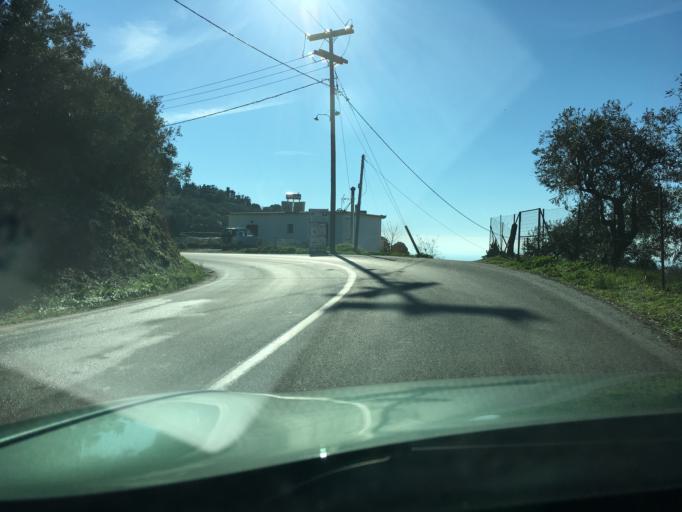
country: GR
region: Thessaly
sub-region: Nomos Magnisias
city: Skopelos
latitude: 39.1747
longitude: 23.6246
